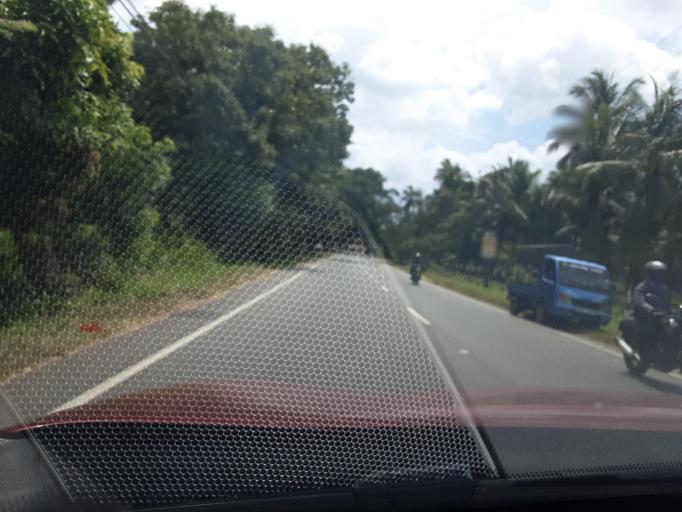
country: LK
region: North Western
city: Kuliyapitiya
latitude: 7.4503
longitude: 80.1836
